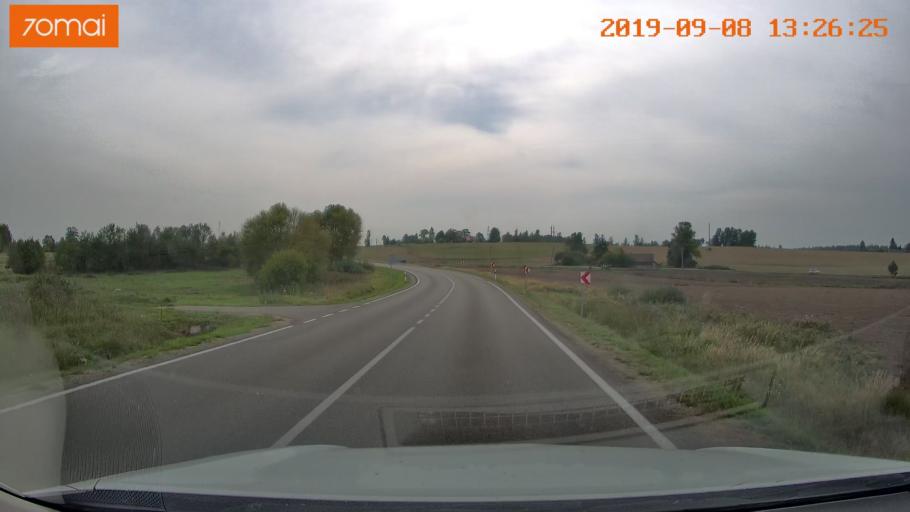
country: LT
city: Jieznas
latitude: 54.5997
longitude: 24.1619
